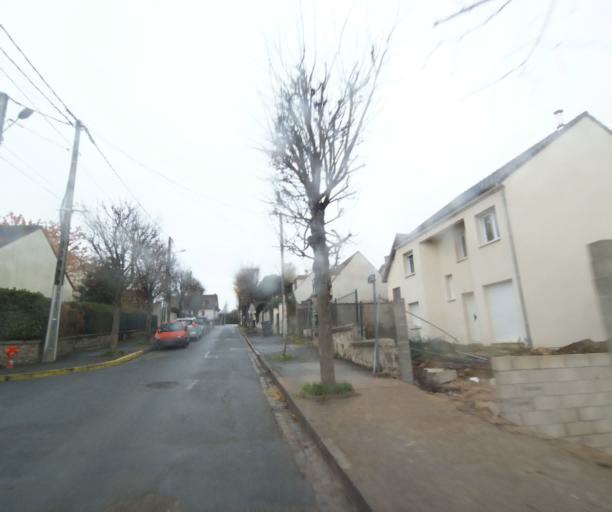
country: FR
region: Ile-de-France
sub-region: Departement de l'Essonne
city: Ris-Orangis
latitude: 48.6477
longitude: 2.4319
